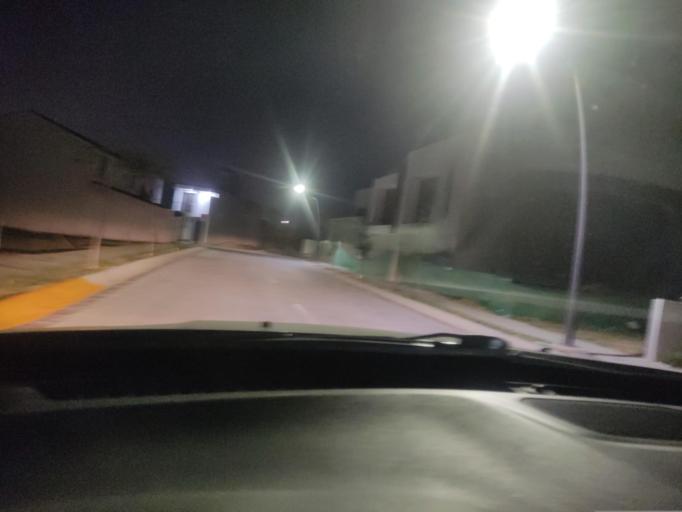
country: MX
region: Guanajuato
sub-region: Leon
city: Ladrilleras del Refugio
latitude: 21.0862
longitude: -101.5620
